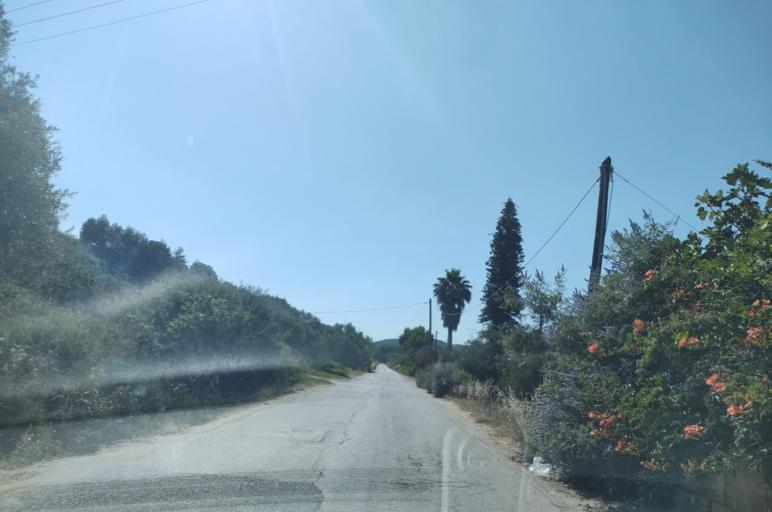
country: GR
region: Crete
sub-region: Nomos Chanias
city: Georgioupolis
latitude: 35.3620
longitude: 24.2473
